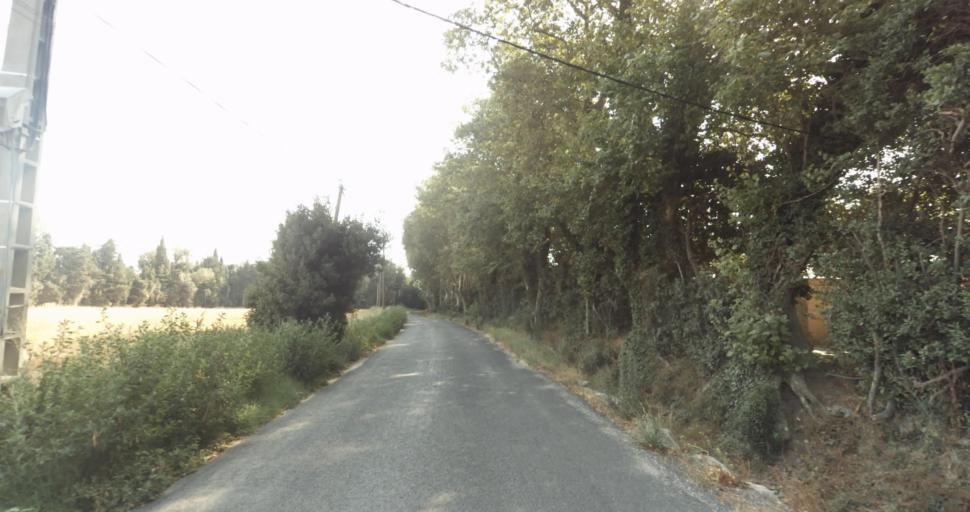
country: FR
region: Languedoc-Roussillon
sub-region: Departement des Pyrenees-Orientales
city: Latour-Bas-Elne
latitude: 42.6061
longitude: 3.0196
